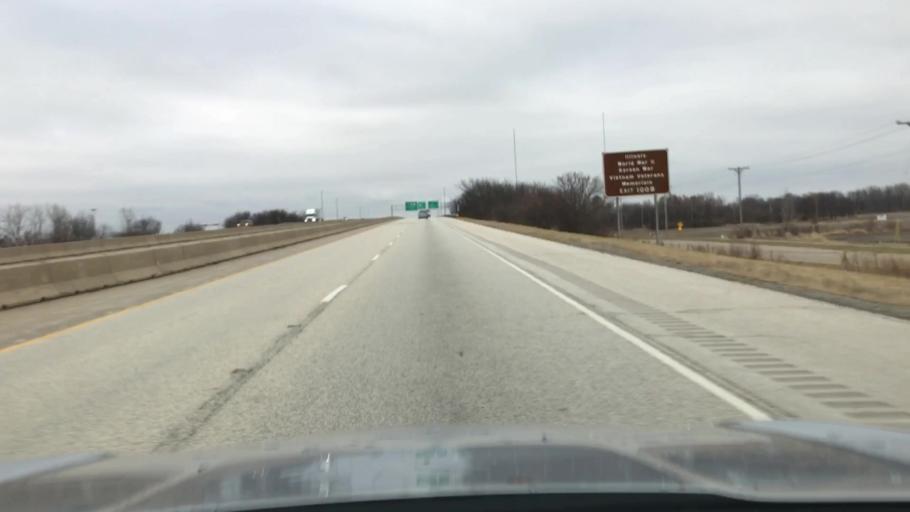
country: US
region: Illinois
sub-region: Sangamon County
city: Grandview
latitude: 39.8384
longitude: -89.5939
